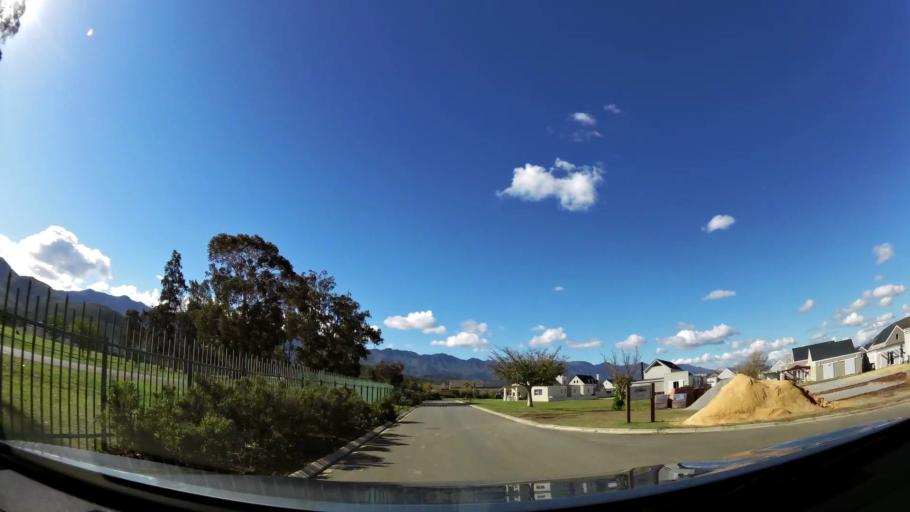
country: ZA
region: Western Cape
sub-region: Cape Winelands District Municipality
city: Ashton
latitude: -33.8105
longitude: 19.8550
